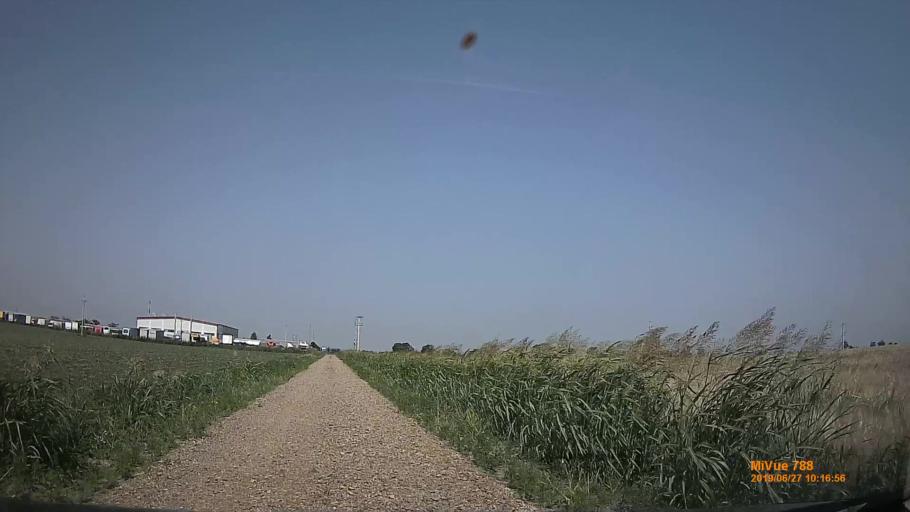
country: HU
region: Pest
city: Cegled
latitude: 47.1974
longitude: 19.8208
